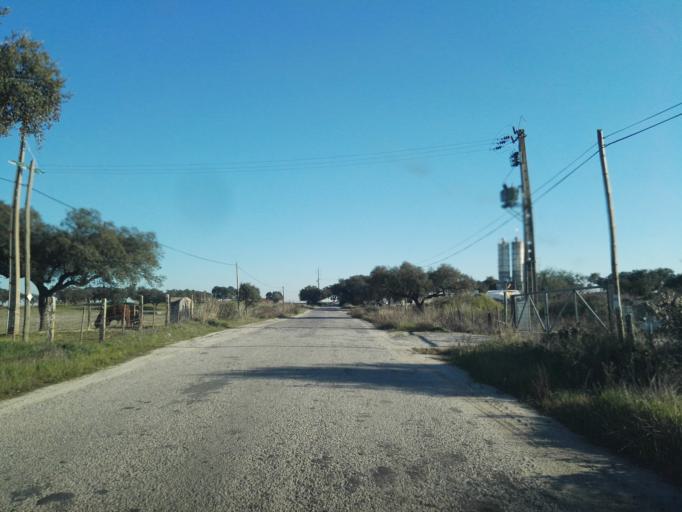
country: PT
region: Evora
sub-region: Evora
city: Evora
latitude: 38.5365
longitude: -7.9527
